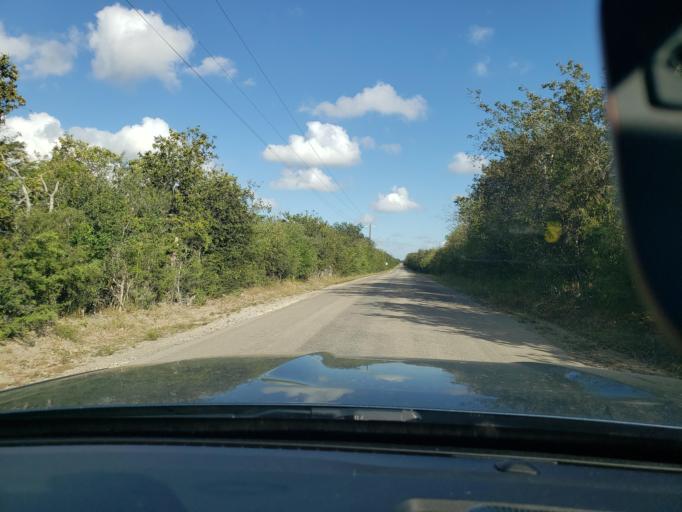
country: US
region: Texas
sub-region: Bee County
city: Beeville
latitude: 28.4476
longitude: -97.7168
